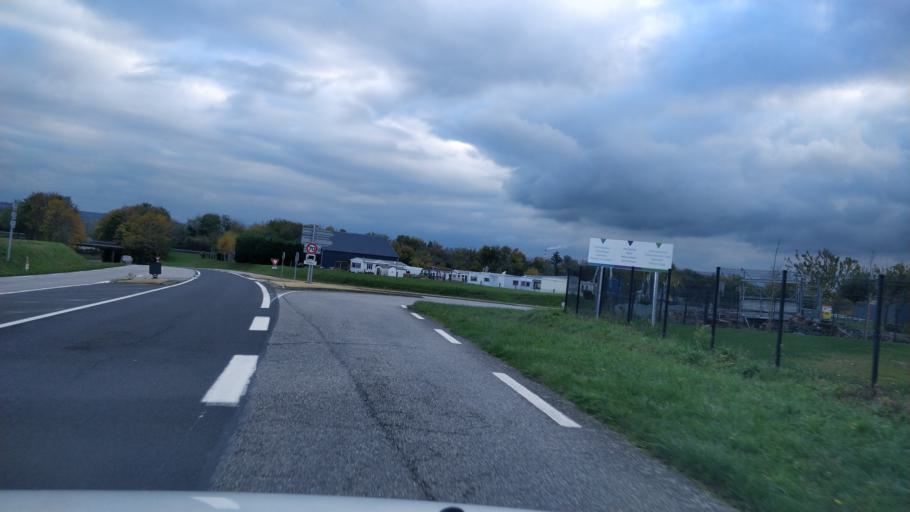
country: FR
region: Lower Normandy
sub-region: Departement du Calvados
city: Benouville
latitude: 49.2511
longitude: -0.2799
